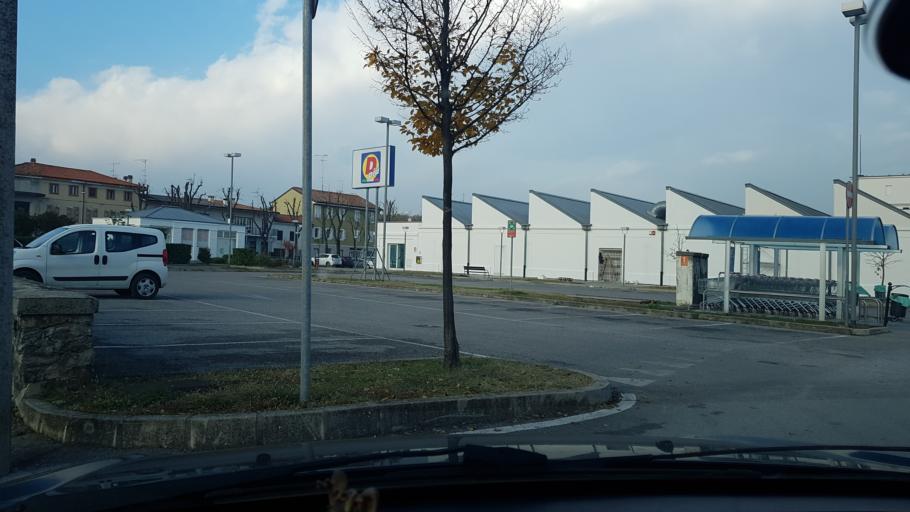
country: IT
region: Friuli Venezia Giulia
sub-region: Provincia di Gorizia
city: Ronchi dei Legionari
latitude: 45.8308
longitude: 13.5058
